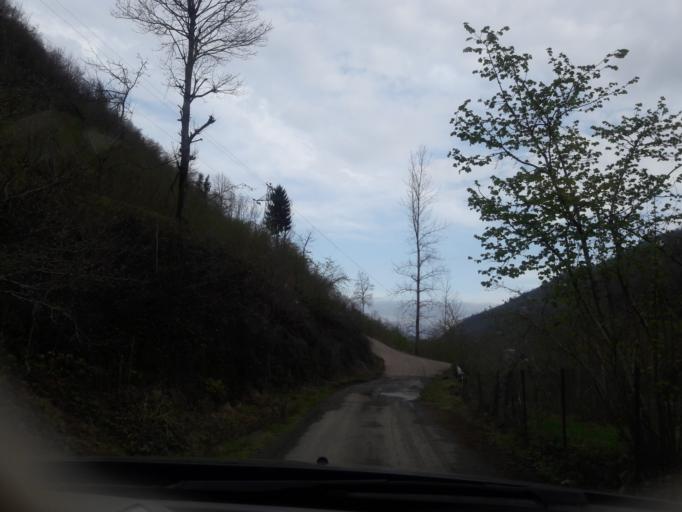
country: TR
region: Trabzon
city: Salpazari
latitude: 40.9699
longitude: 39.1973
